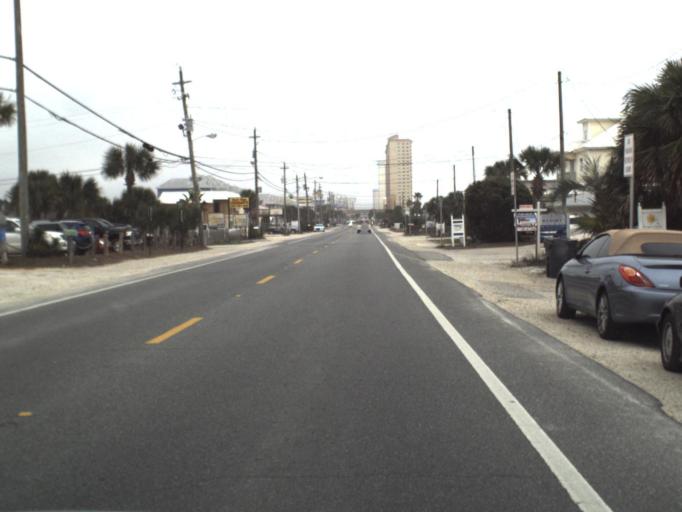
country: US
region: Florida
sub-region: Bay County
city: Laguna Beach
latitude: 30.2185
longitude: -85.8821
